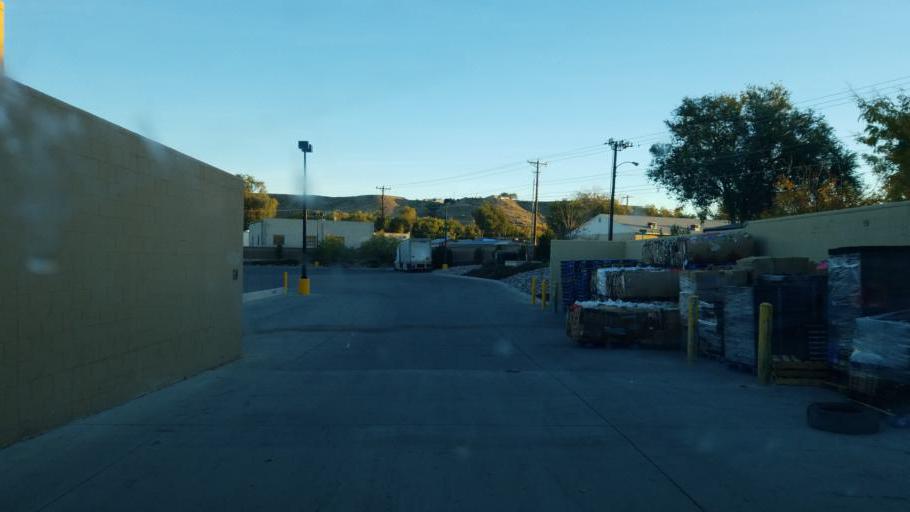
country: US
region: New Mexico
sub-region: San Juan County
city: Farmington
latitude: 36.7317
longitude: -108.2254
